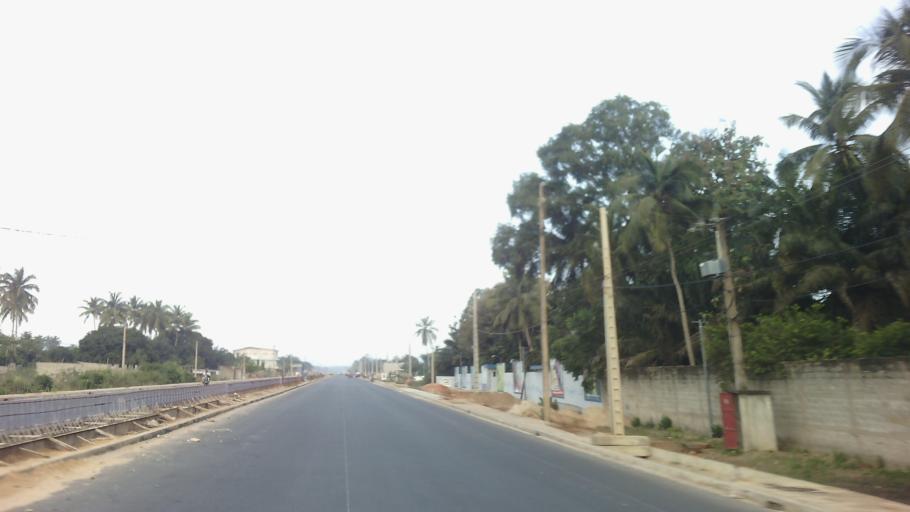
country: BJ
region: Atlantique
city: Hevie
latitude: 6.3842
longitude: 2.1950
